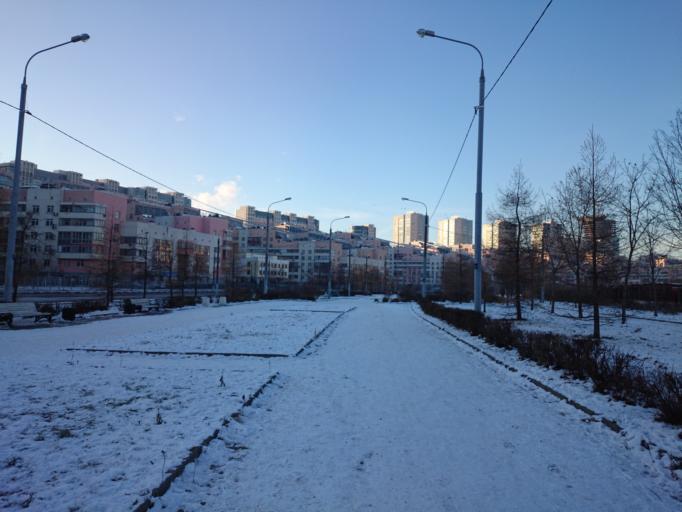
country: RU
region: Moscow
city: Sokol
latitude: 55.7853
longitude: 37.5292
